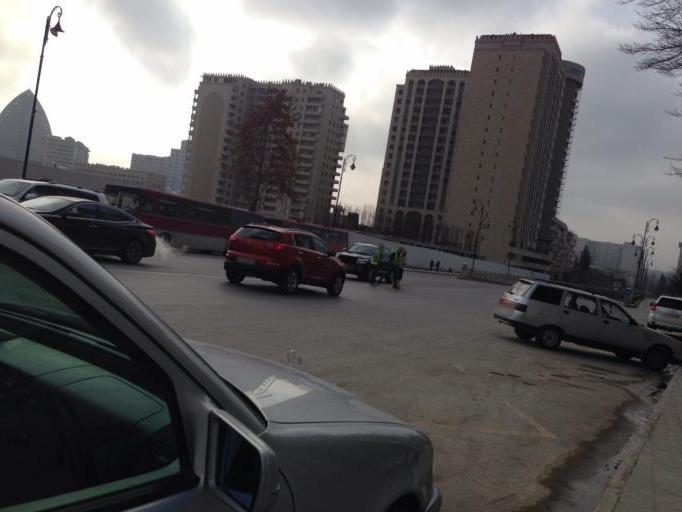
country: AZ
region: Baki
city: Baku
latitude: 40.3969
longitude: 49.8628
